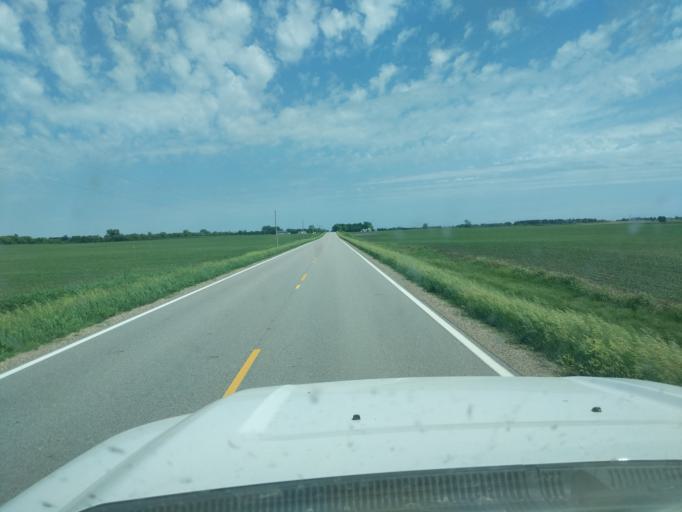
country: US
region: Minnesota
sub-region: Yellow Medicine County
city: Granite Falls
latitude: 44.7541
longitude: -95.4014
